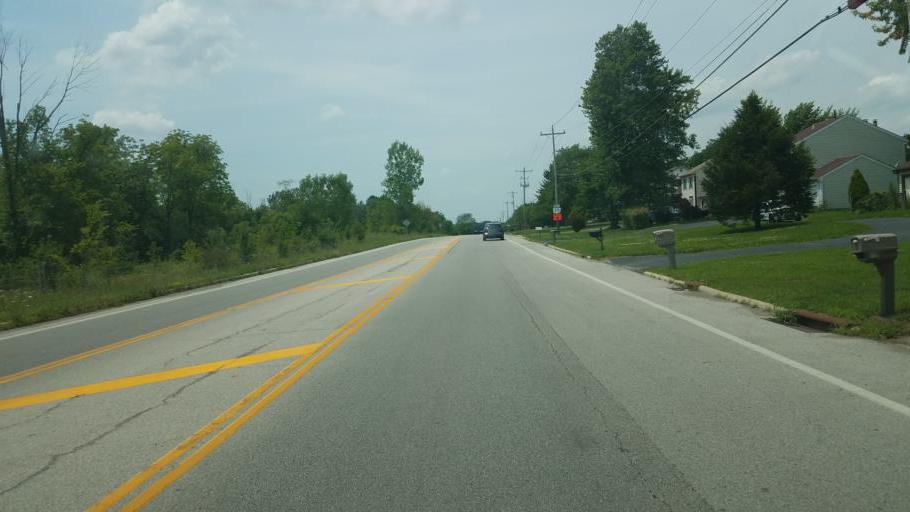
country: US
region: Ohio
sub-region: Delaware County
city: Lewis Center
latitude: 40.1571
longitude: -83.0236
